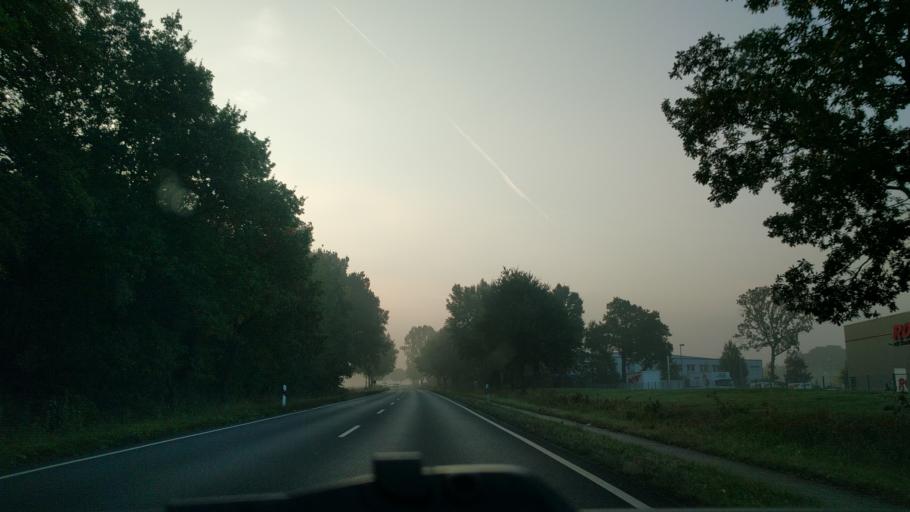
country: DE
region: Lower Saxony
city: Isenbuttel
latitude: 52.4458
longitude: 10.5918
